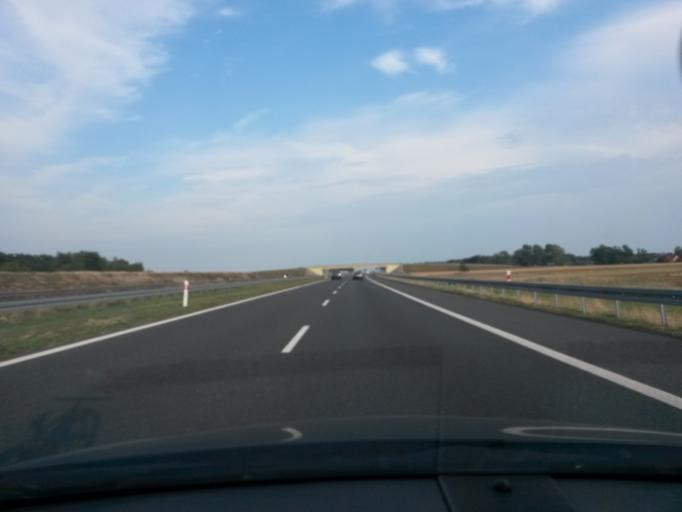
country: PL
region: Lodz Voivodeship
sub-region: Powiat zgierski
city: Parzeczew
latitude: 51.9503
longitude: 19.1605
